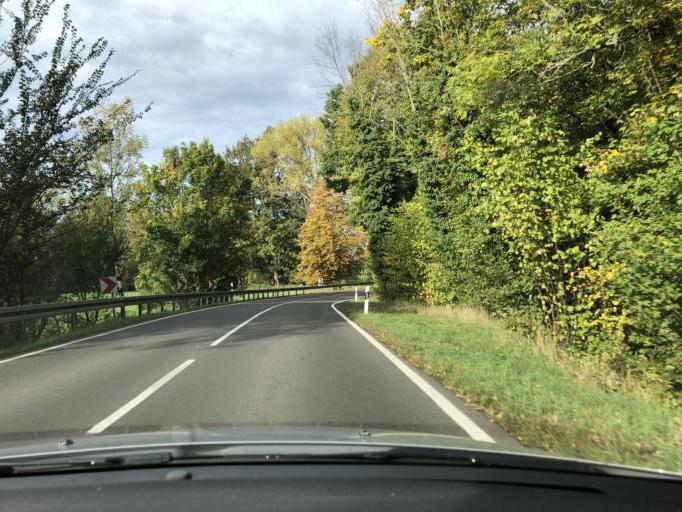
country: DE
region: Saxony
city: Groitzsch
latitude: 51.1724
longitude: 12.2847
